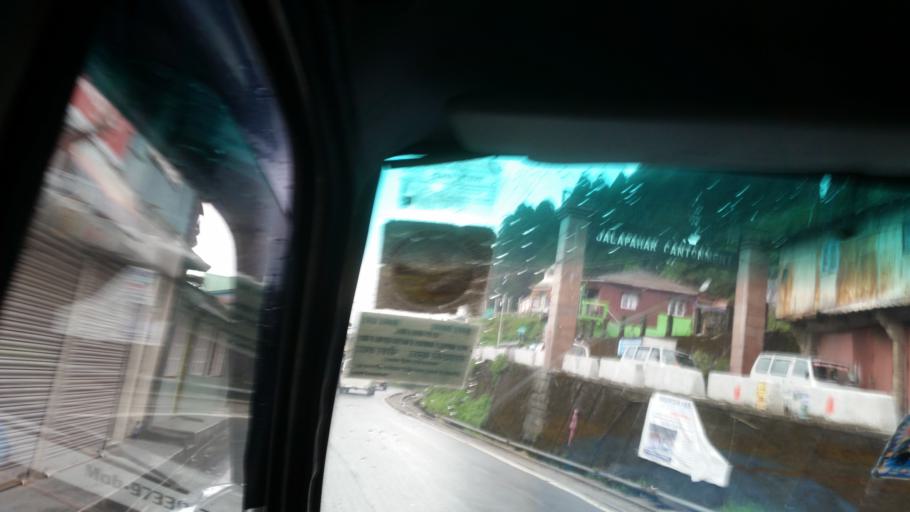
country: IN
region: West Bengal
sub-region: Darjiling
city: Darjiling
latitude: 27.0087
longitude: 88.2587
